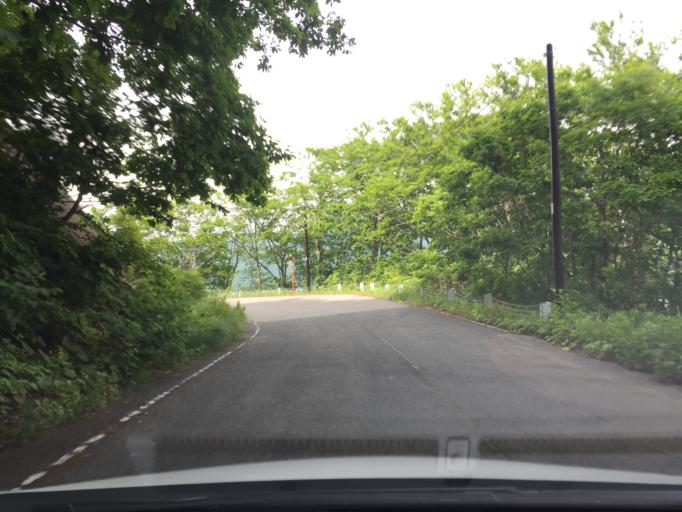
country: JP
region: Fukushima
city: Inawashiro
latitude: 37.7117
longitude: 140.0434
